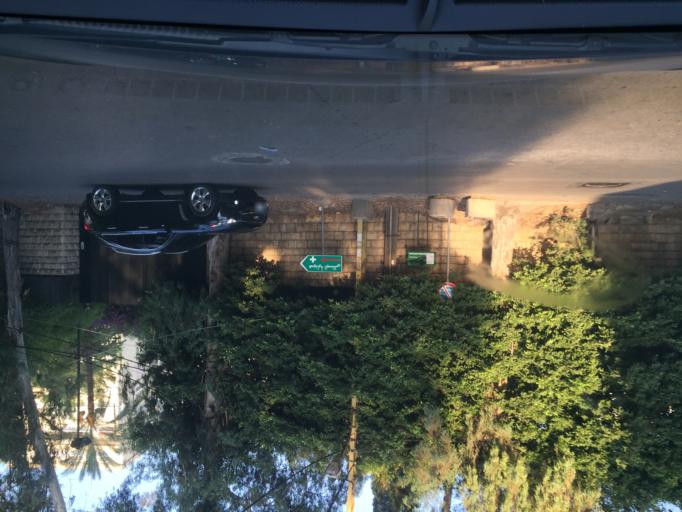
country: LB
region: Mont-Liban
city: Djounie
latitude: 33.9942
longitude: 35.6421
